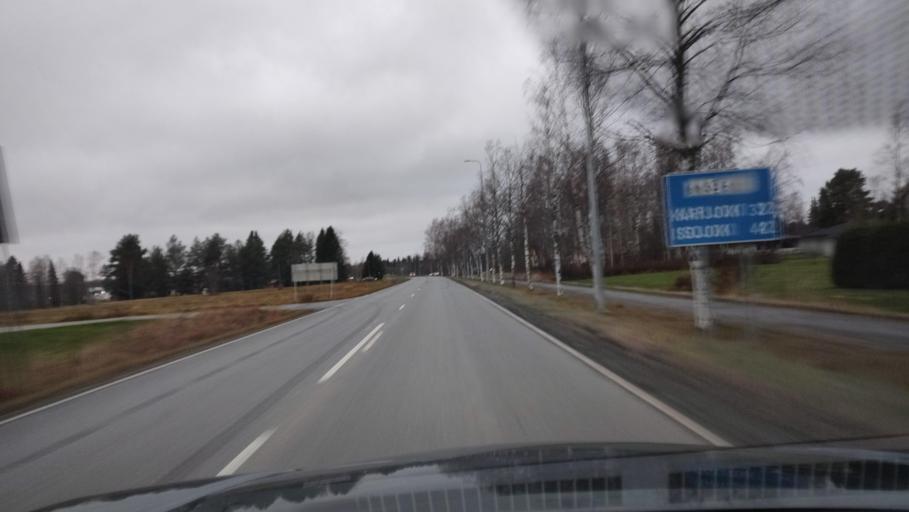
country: FI
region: Southern Ostrobothnia
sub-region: Suupohja
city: Kauhajoki
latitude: 62.4182
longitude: 22.1962
